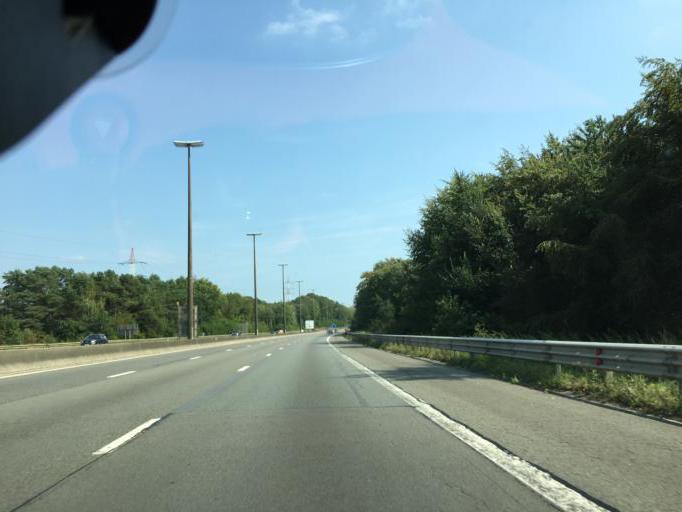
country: BE
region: Wallonia
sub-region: Province du Hainaut
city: Manage
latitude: 50.4982
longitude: 4.2414
